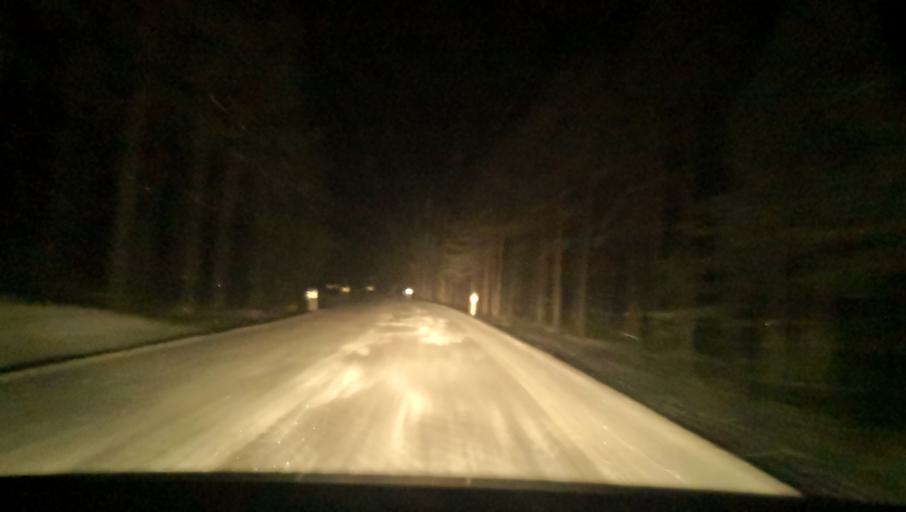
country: SE
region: Uppsala
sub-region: Heby Kommun
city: Tarnsjo
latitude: 60.1190
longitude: 16.8847
